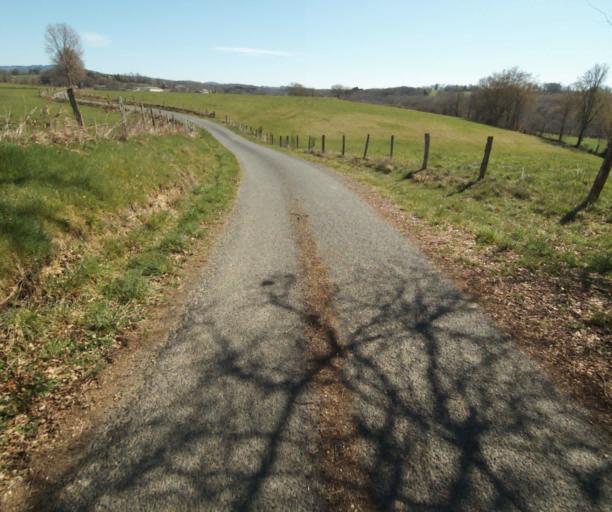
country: FR
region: Limousin
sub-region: Departement de la Correze
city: Chamboulive
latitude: 45.4573
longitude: 1.6902
